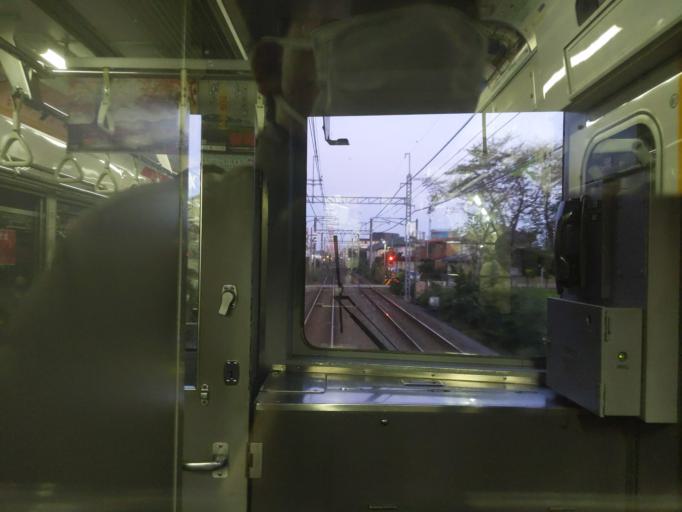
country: JP
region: Chiba
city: Kashiwa
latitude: 35.8603
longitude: 139.9597
